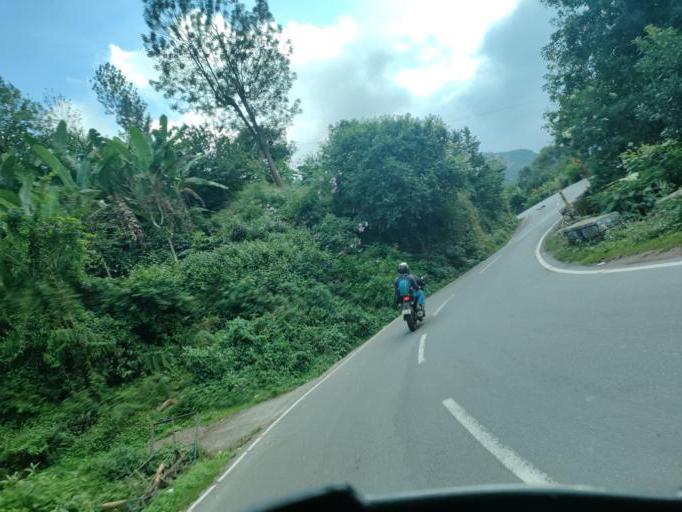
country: IN
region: Tamil Nadu
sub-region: Dindigul
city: Kodaikanal
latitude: 10.2614
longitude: 77.5362
